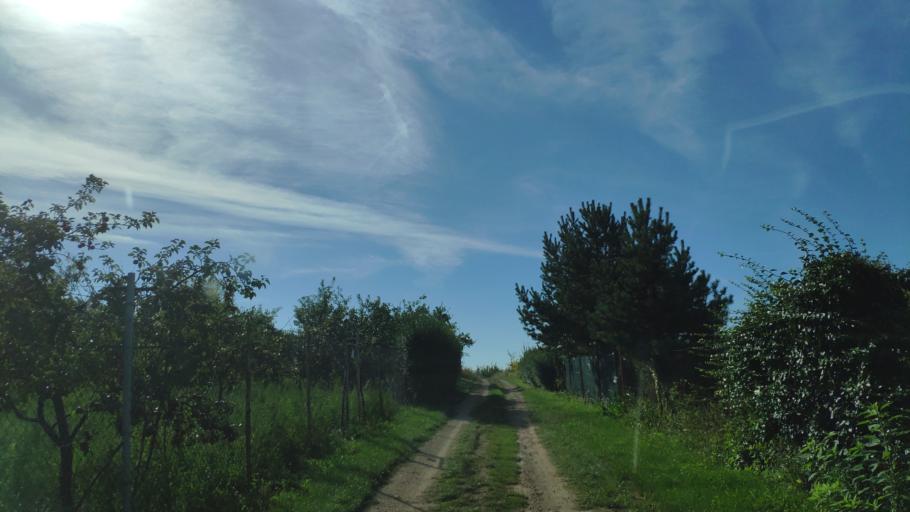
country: SK
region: Kosicky
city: Kosice
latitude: 48.7682
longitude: 21.2485
